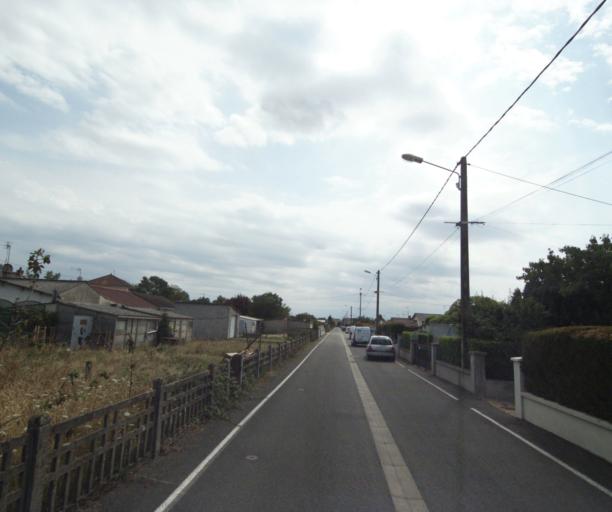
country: FR
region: Bourgogne
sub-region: Departement de Saone-et-Loire
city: Gueugnon
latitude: 46.6084
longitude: 4.0540
